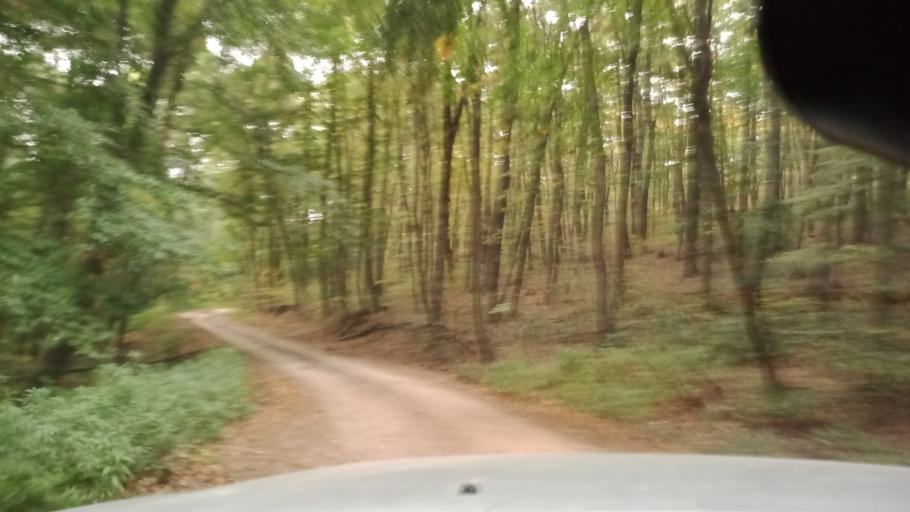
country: HU
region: Fejer
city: Mor
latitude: 47.3801
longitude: 18.2630
